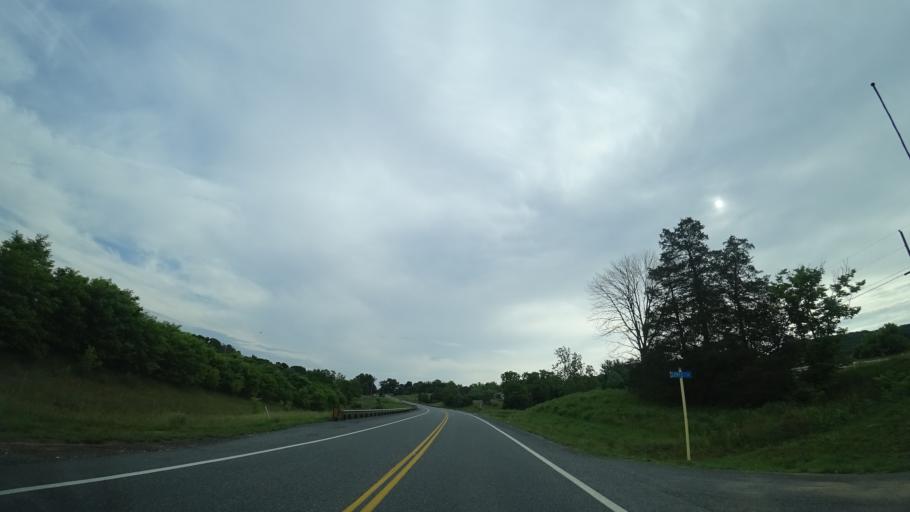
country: US
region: Virginia
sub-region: Page County
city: Luray
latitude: 38.7861
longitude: -78.3652
